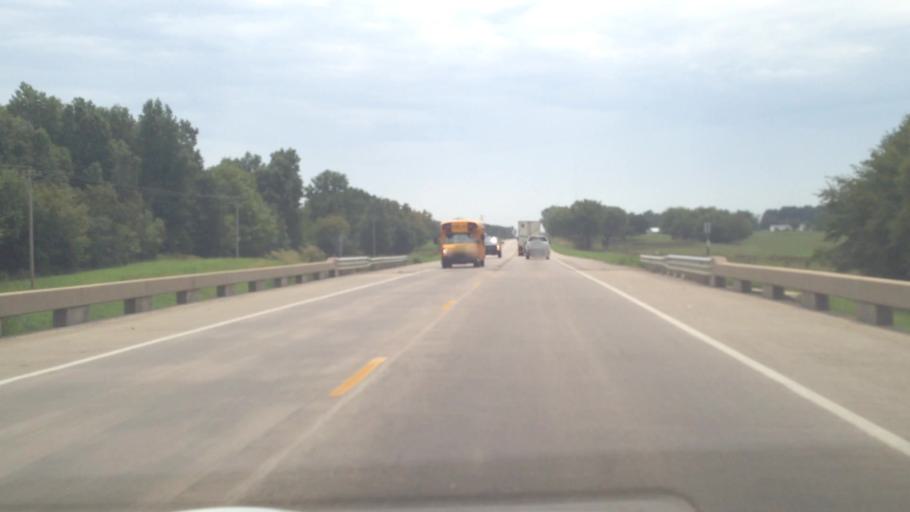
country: US
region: Kansas
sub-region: Crawford County
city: Pittsburg
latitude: 37.2556
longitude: -94.7052
